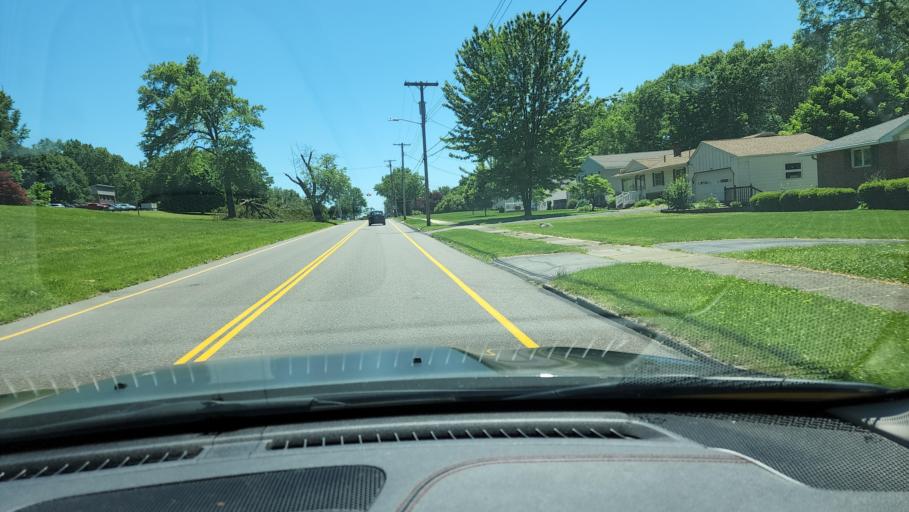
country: US
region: Ohio
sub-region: Trumbull County
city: Niles
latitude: 41.1901
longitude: -80.7448
